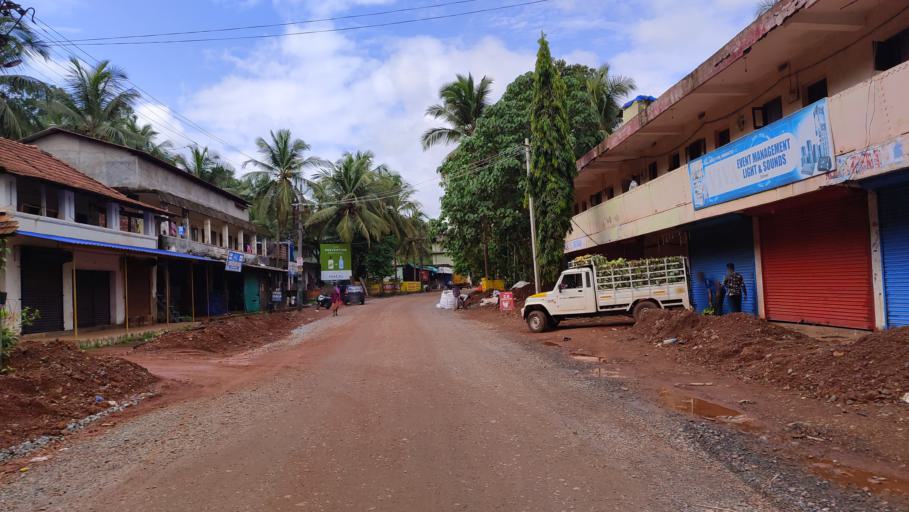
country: IN
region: Kerala
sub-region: Kasaragod District
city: Kasaragod
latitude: 12.5211
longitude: 75.0720
